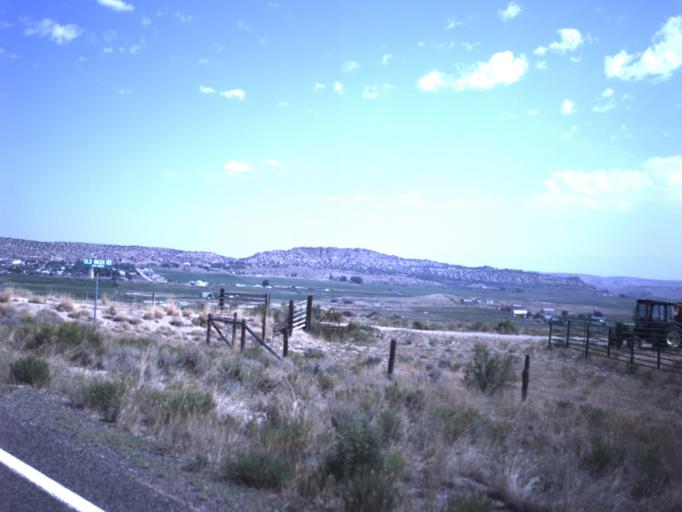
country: US
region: Utah
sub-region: Daggett County
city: Manila
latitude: 40.9686
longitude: -109.7136
